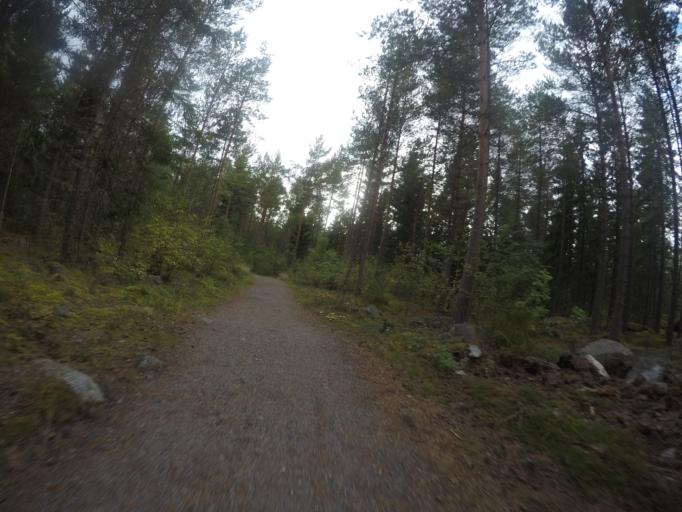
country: SE
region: Vaestmanland
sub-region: Vasteras
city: Vasteras
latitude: 59.6654
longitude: 16.5214
